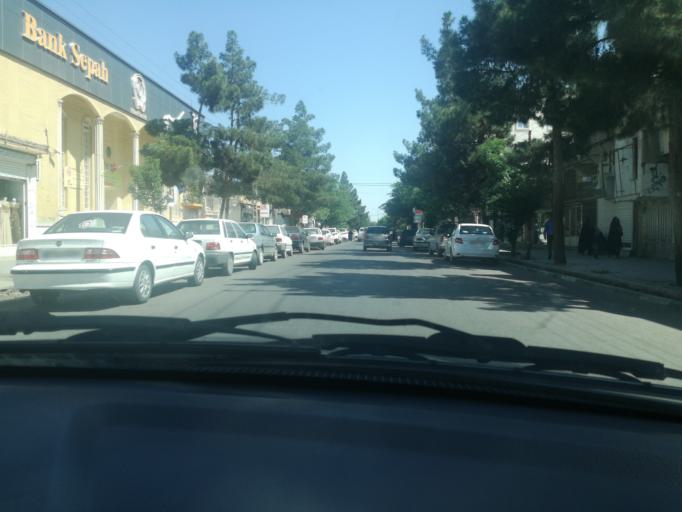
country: IR
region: Razavi Khorasan
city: Sarakhs
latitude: 36.5380
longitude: 61.1634
